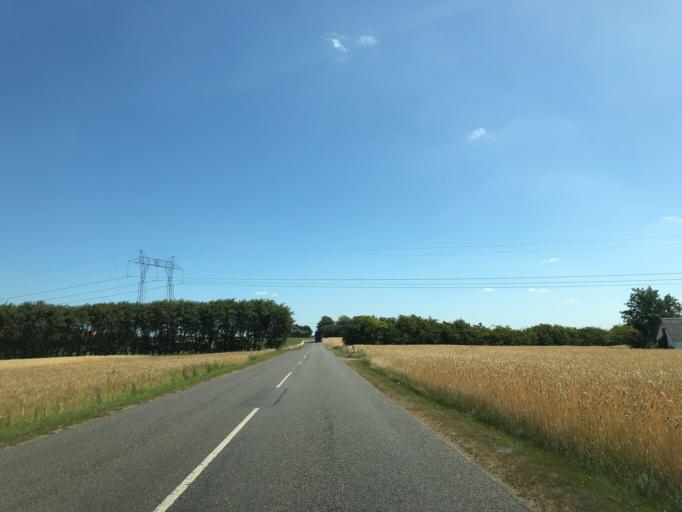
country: DK
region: North Denmark
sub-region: Vesthimmerland Kommune
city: Alestrup
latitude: 56.5767
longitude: 9.5603
